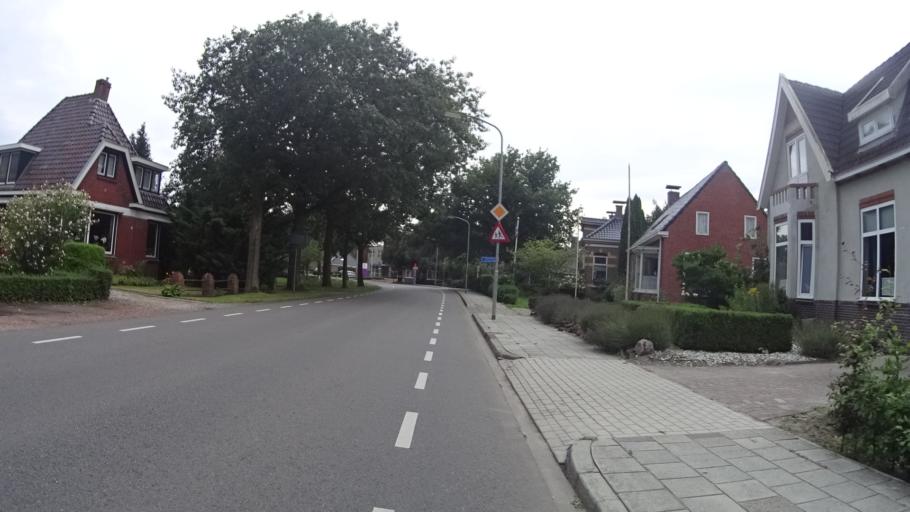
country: NL
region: Groningen
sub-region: Gemeente Slochteren
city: Slochteren
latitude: 53.2213
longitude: 6.8059
